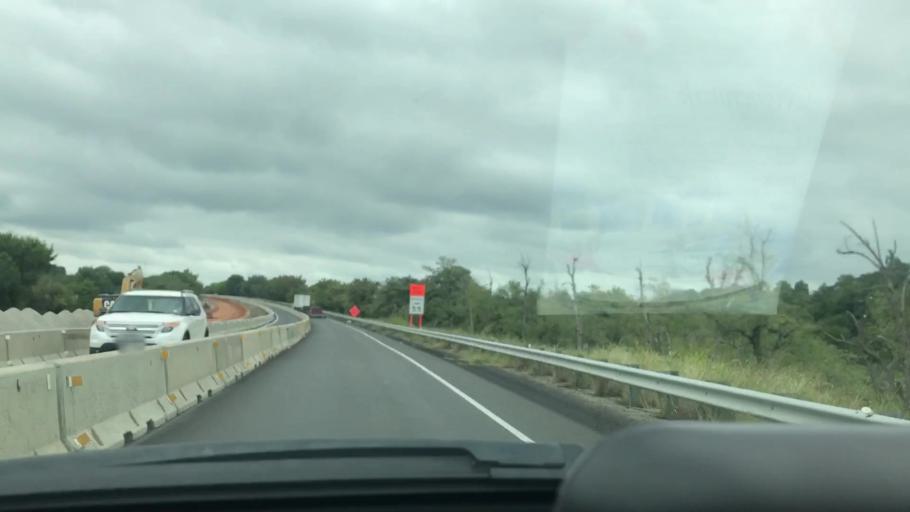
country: US
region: Oklahoma
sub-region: McIntosh County
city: Eufaula
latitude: 35.2484
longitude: -95.5850
